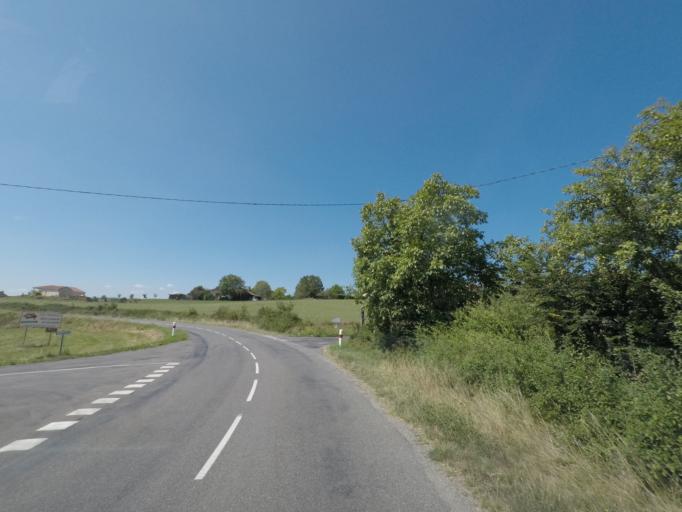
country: FR
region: Midi-Pyrenees
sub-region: Departement de l'Aveyron
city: Capdenac-Gare
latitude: 44.6149
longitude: 2.0866
